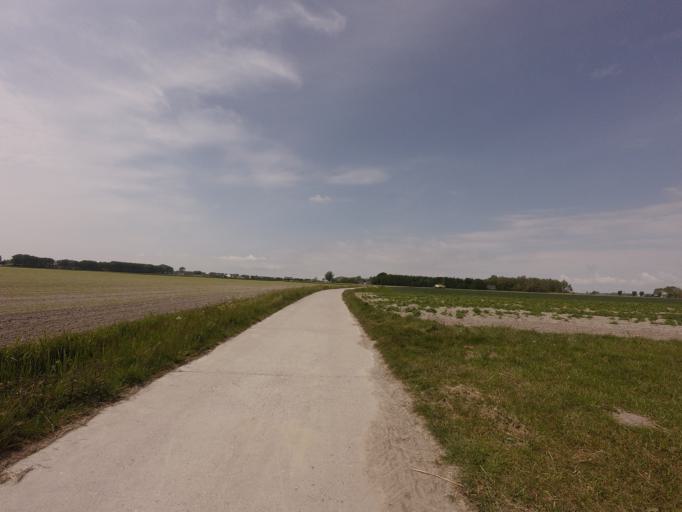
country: NL
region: Friesland
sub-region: Sudwest Fryslan
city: Bolsward
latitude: 53.1067
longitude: 5.4874
